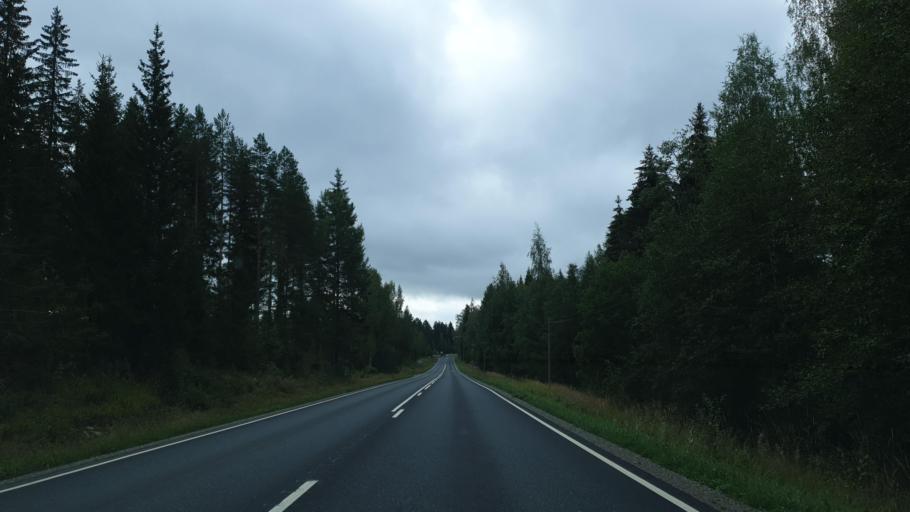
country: FI
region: Northern Savo
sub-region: Koillis-Savo
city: Juankoski
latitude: 63.2079
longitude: 28.2741
